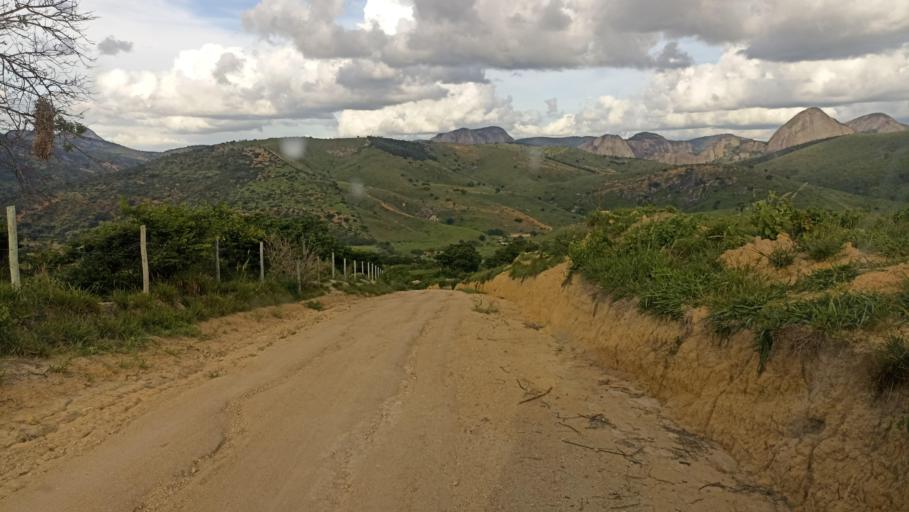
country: BR
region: Minas Gerais
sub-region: Almenara
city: Almenara
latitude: -16.5441
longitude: -40.4486
